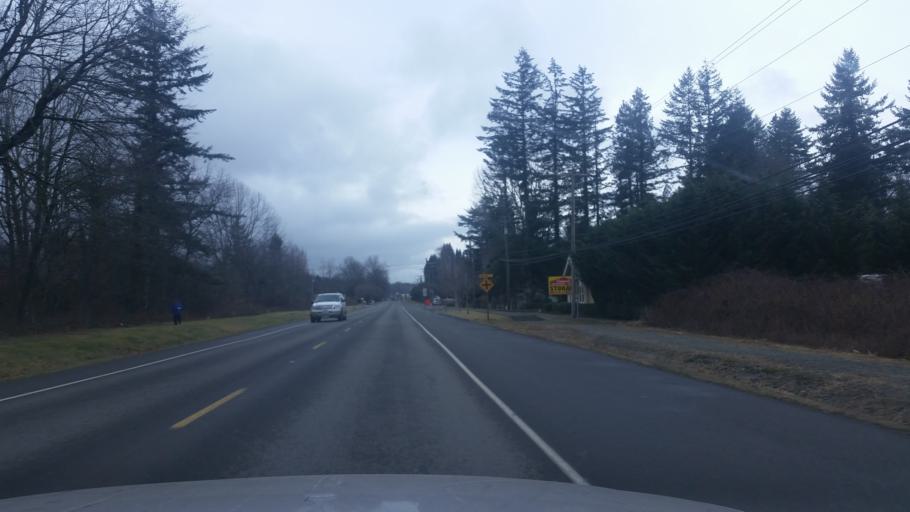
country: US
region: Washington
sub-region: King County
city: North Bend
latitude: 47.4880
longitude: -121.7720
